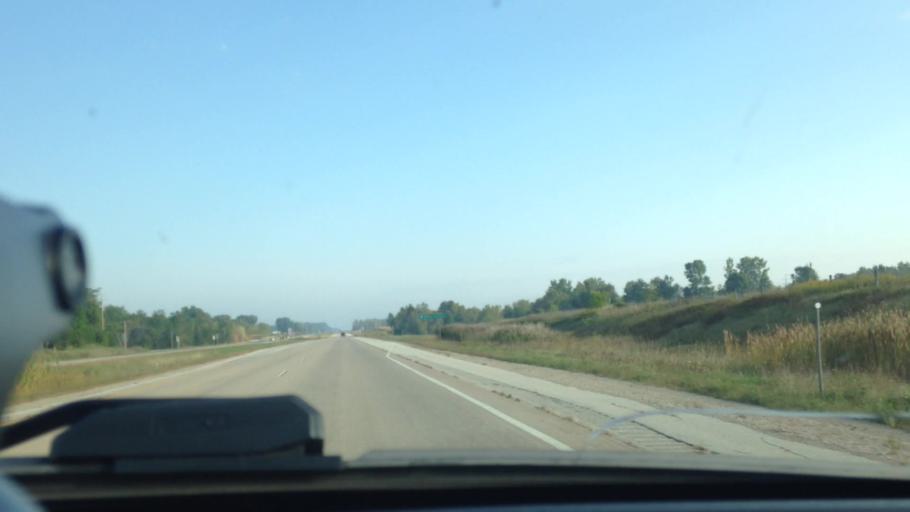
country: US
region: Wisconsin
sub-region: Oconto County
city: Oconto Falls
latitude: 45.0061
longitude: -88.0450
